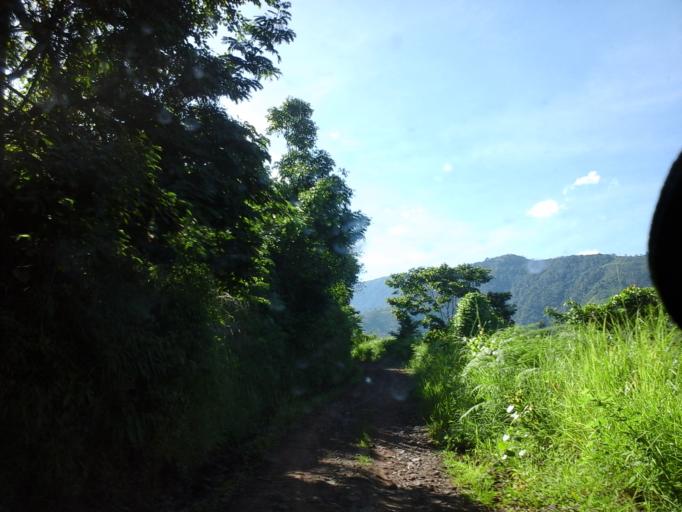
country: CO
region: Cesar
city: San Diego
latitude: 10.2687
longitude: -73.0809
